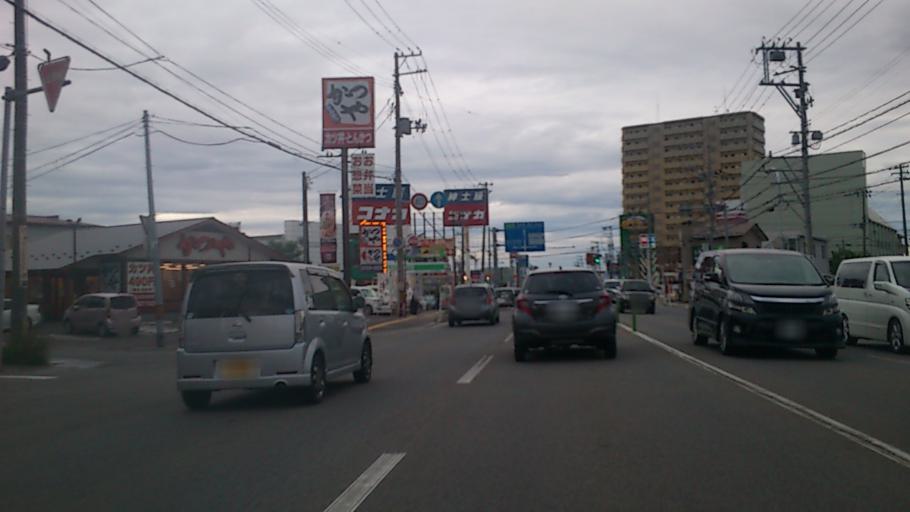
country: JP
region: Akita
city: Akita Shi
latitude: 39.7381
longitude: 140.0969
